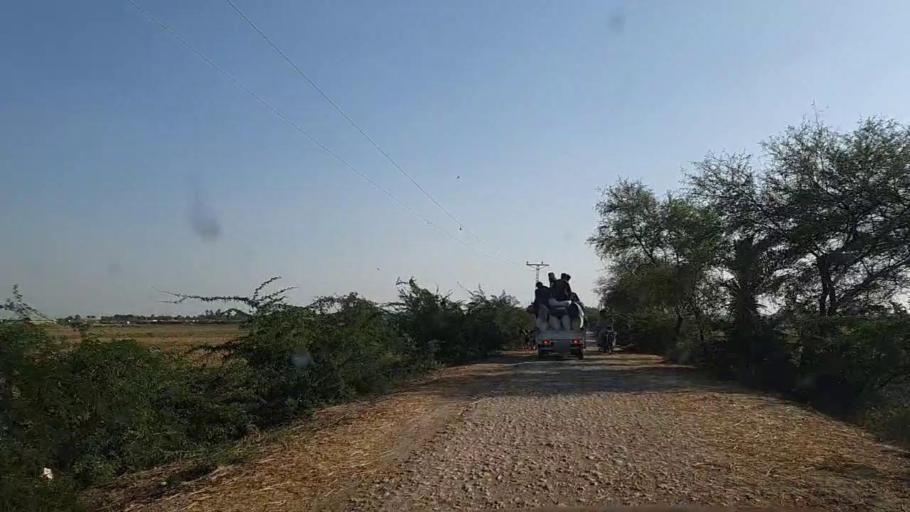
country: PK
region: Sindh
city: Thatta
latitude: 24.6167
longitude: 68.0781
